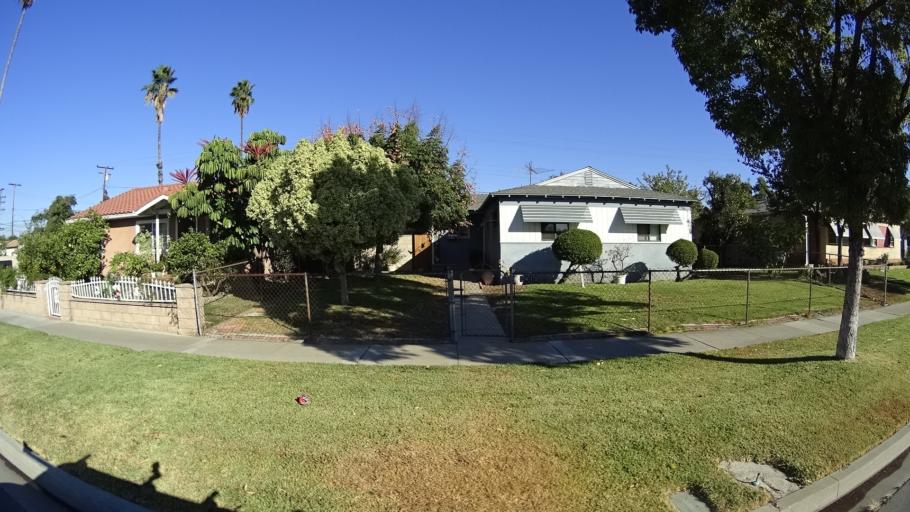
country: US
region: California
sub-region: Orange County
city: Fullerton
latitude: 33.8472
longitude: -117.9380
